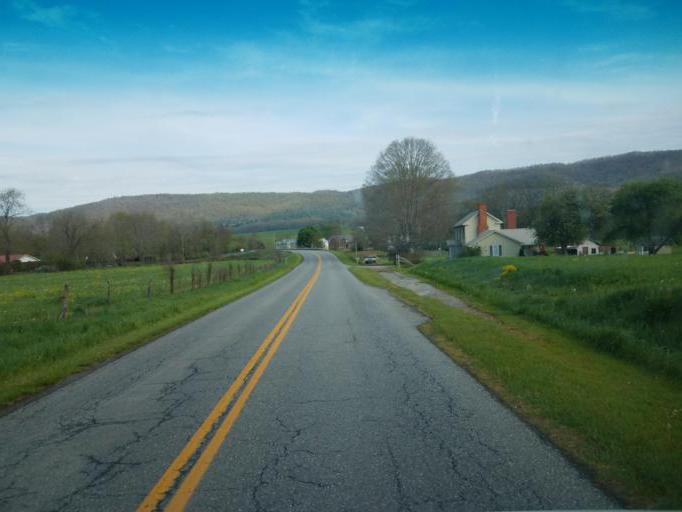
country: US
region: Virginia
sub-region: Smyth County
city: Marion
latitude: 36.7715
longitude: -81.4501
